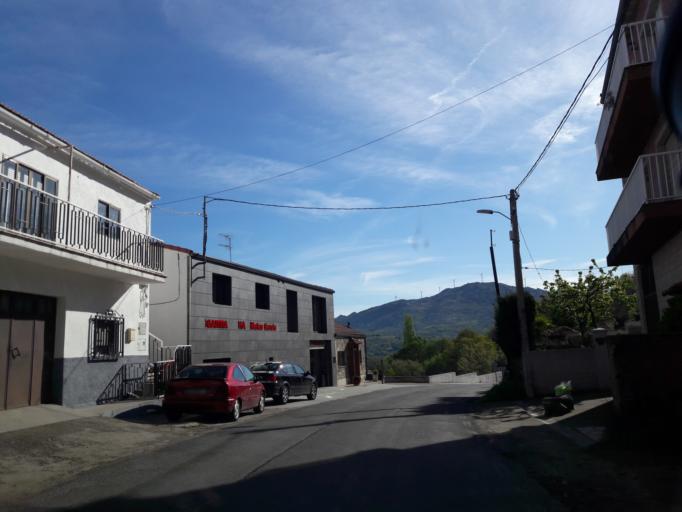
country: ES
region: Castille and Leon
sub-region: Provincia de Salamanca
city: Sanchotello
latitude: 40.4399
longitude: -5.7500
